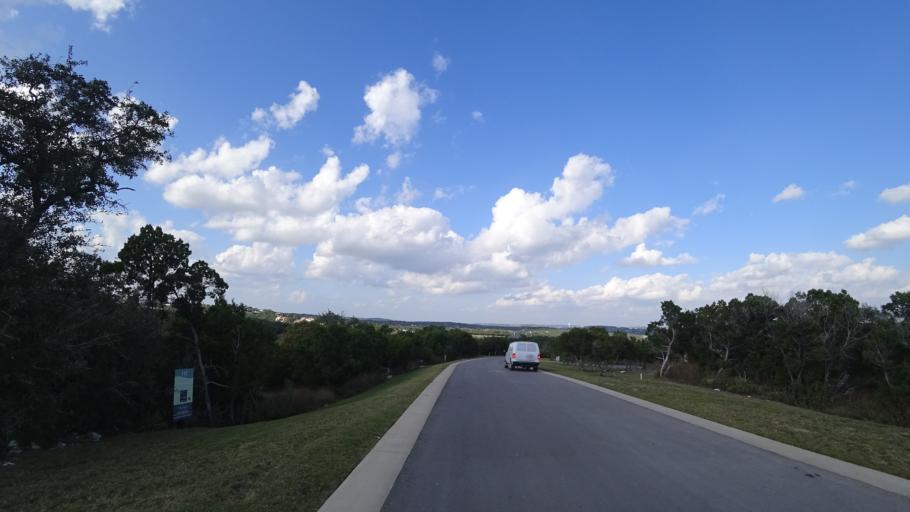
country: US
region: Texas
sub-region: Travis County
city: Barton Creek
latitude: 30.2633
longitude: -97.8748
